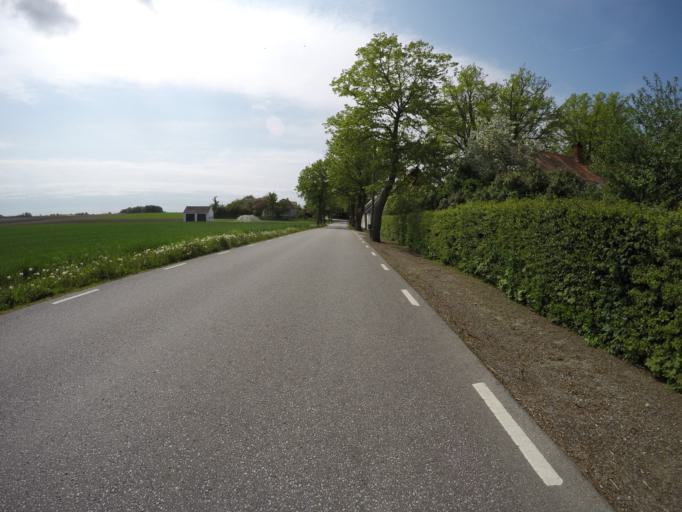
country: SE
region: Skane
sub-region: Malmo
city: Tygelsjo
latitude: 55.5426
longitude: 13.0236
